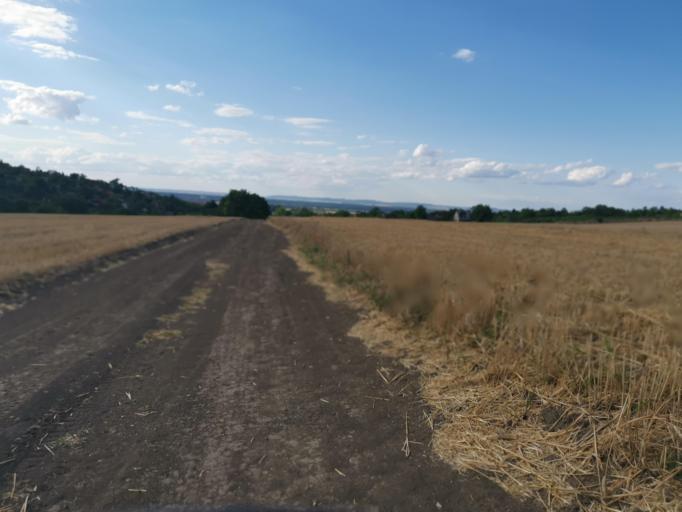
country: SK
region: Trnavsky
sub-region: Okres Skalica
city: Skalica
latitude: 48.8286
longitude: 17.2536
